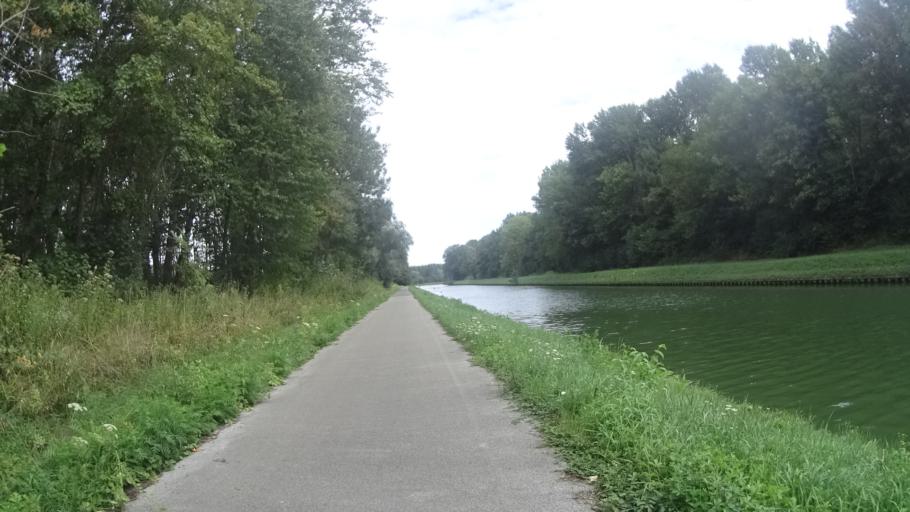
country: FR
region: Picardie
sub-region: Departement de l'Oise
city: Noyon
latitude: 49.5750
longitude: 3.0659
